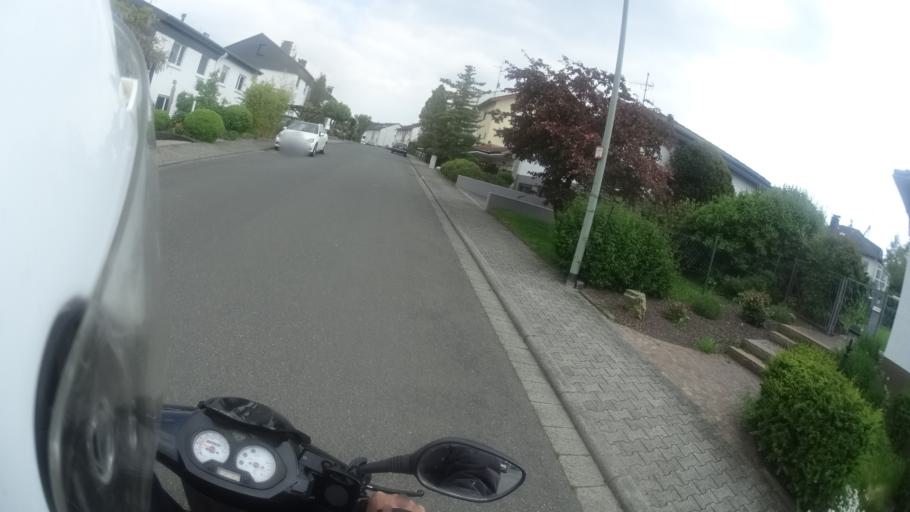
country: DE
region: Hesse
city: Taunusstein
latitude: 50.1301
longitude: 8.1399
